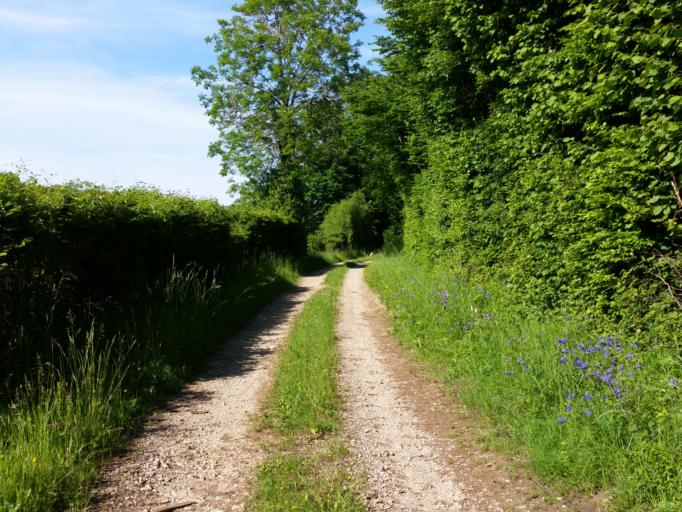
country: FR
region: Franche-Comte
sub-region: Departement du Doubs
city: Quingey
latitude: 47.0444
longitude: 5.9732
